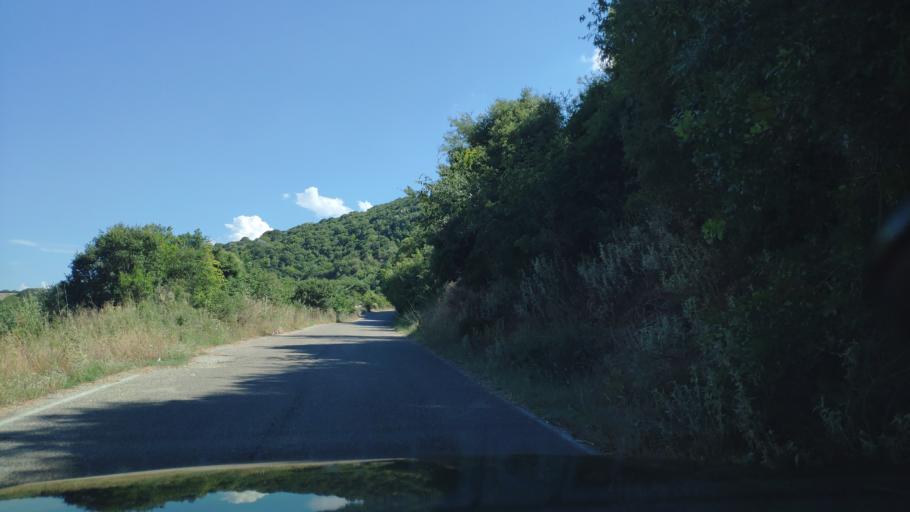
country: GR
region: West Greece
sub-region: Nomos Aitolias kai Akarnanias
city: Katouna
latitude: 38.8266
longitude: 21.0996
